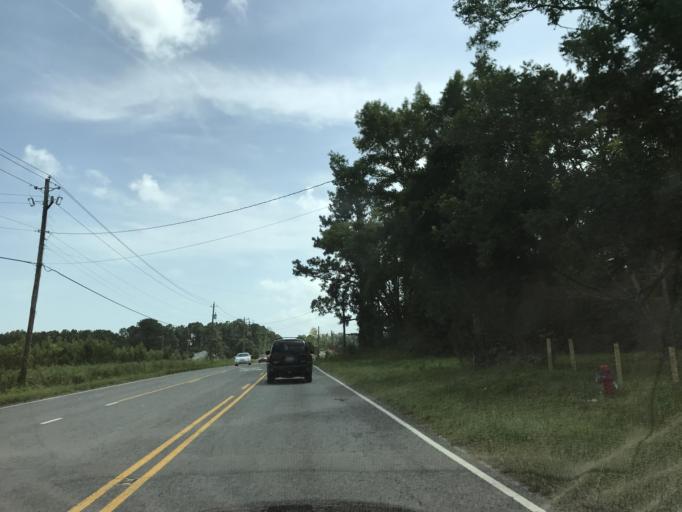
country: US
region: North Carolina
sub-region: New Hanover County
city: Wrightsboro
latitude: 34.3068
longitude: -77.9219
